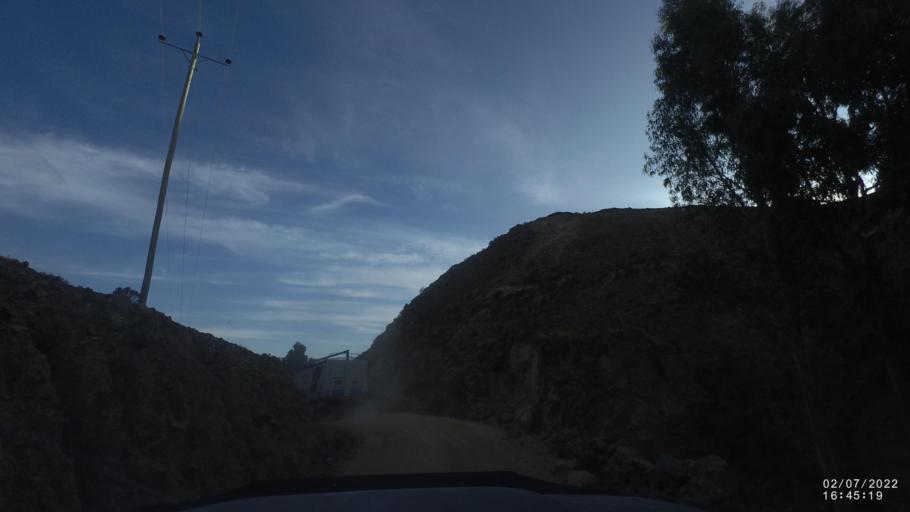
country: BO
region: Cochabamba
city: Irpa Irpa
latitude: -17.9758
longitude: -66.5104
